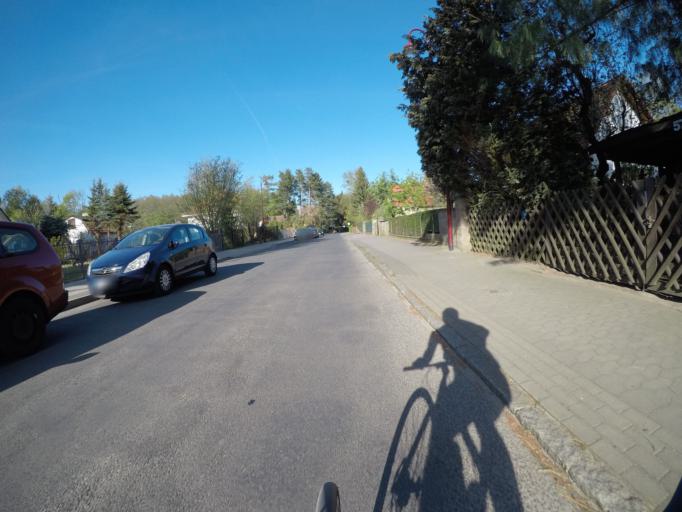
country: DE
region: Brandenburg
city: Neuenhagen
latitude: 52.5160
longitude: 13.6959
